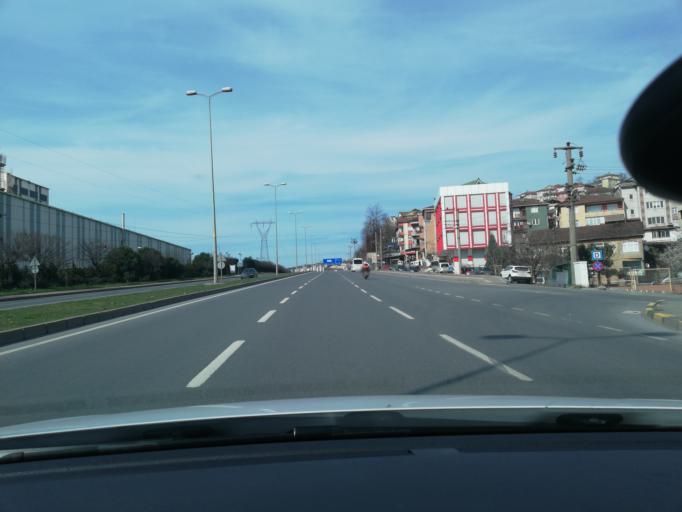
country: TR
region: Zonguldak
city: Eregli
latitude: 41.2622
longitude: 31.4354
